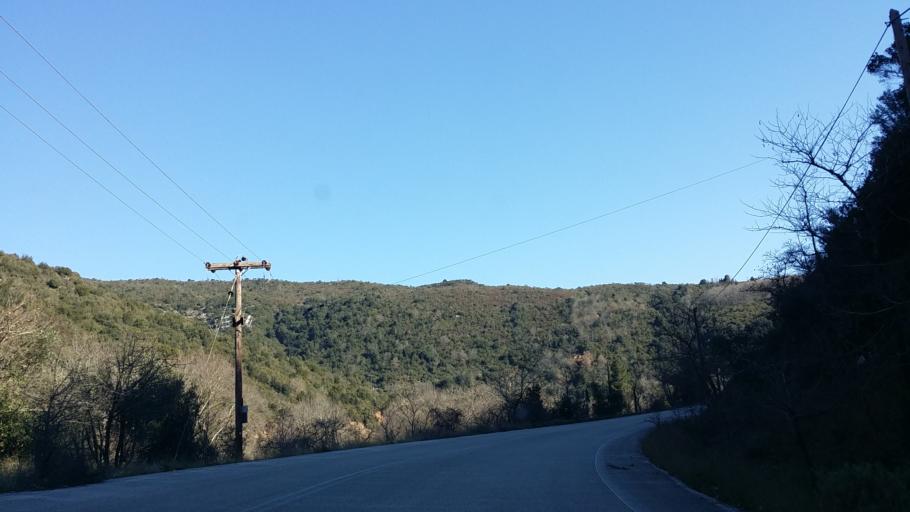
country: GR
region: West Greece
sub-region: Nomos Aitolias kai Akarnanias
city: Sardinia
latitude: 38.9245
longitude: 21.3539
